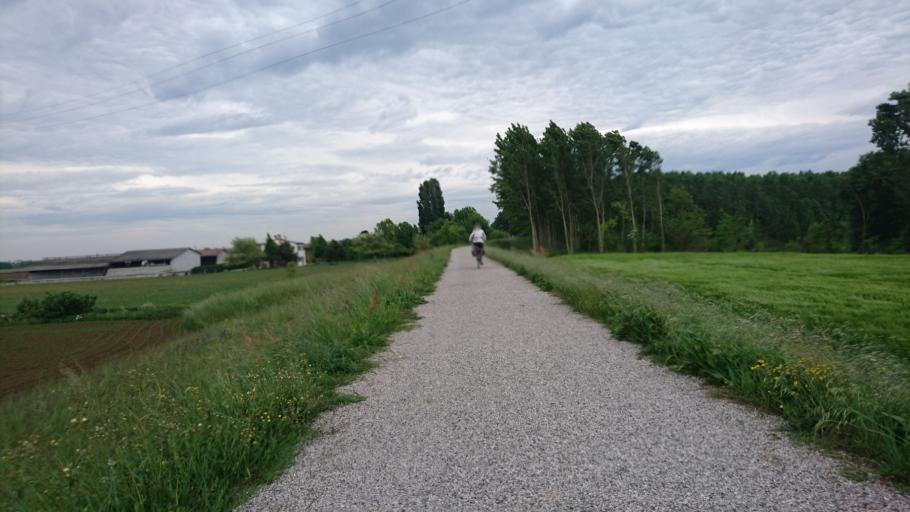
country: IT
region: Veneto
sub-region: Provincia di Padova
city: Saccolongo
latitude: 45.4086
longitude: 11.7510
